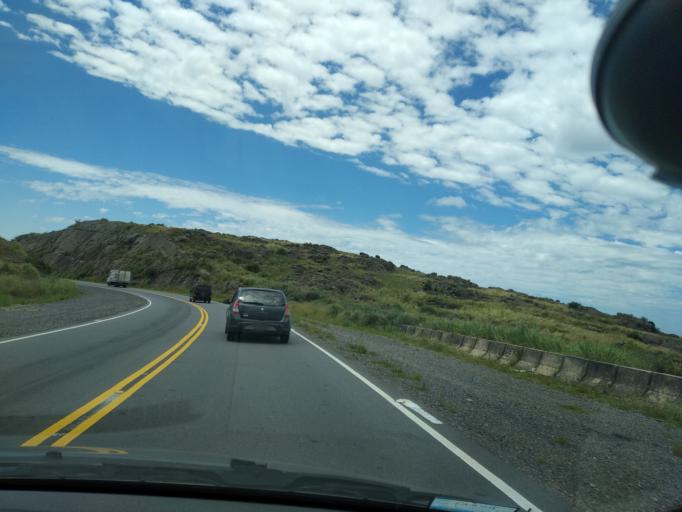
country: AR
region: Cordoba
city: Cuesta Blanca
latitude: -31.6378
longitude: -64.6800
